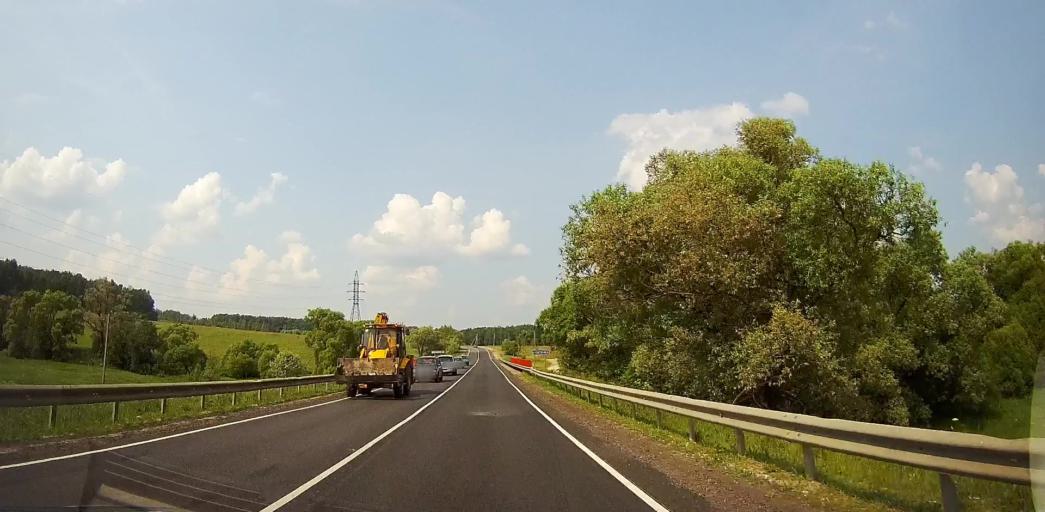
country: RU
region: Moskovskaya
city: Stupino
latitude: 54.9448
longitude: 38.1340
